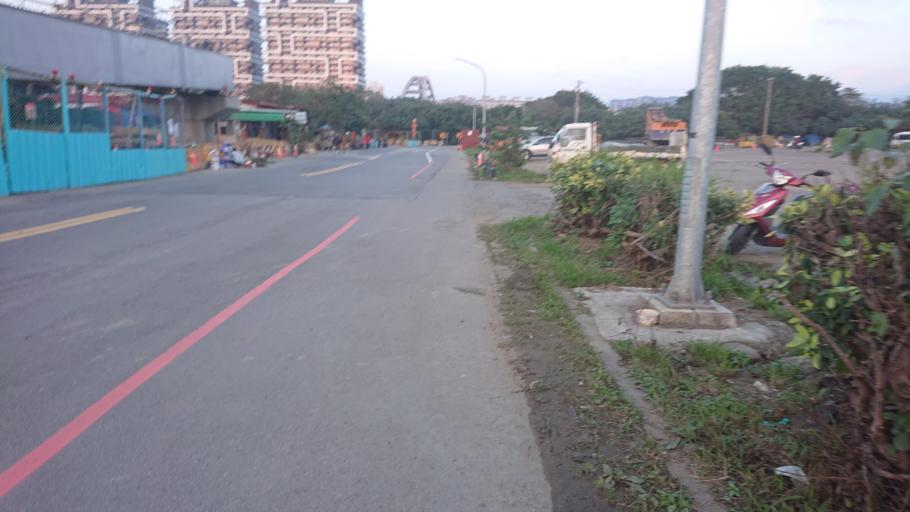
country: TW
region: Taipei
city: Taipei
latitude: 25.1883
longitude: 121.4185
